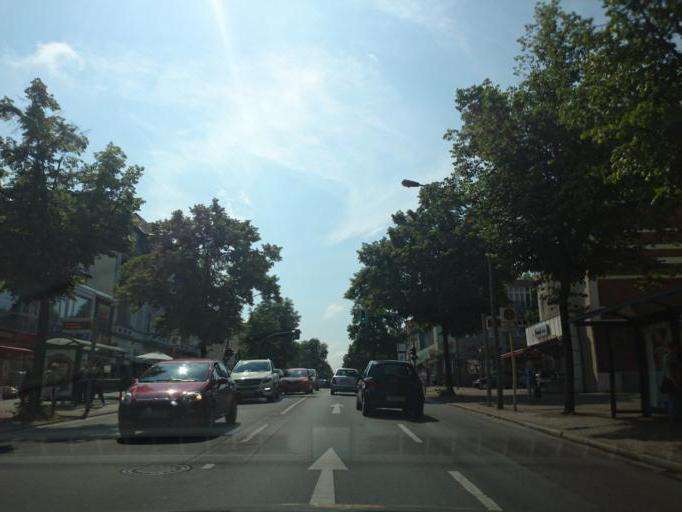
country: DE
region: Berlin
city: Lichterfelde
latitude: 52.4434
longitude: 13.2962
